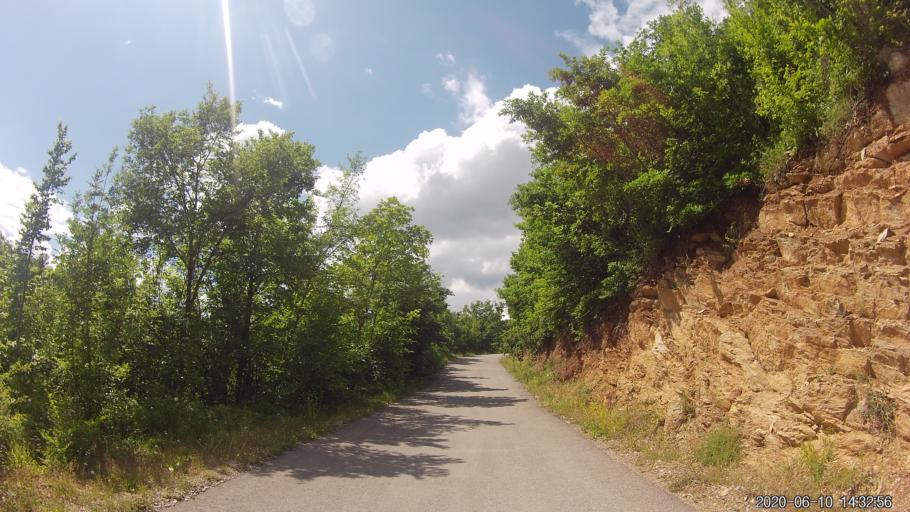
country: XK
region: Prizren
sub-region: Komuna e Therandes
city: Budakovo
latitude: 42.4147
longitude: 20.9273
